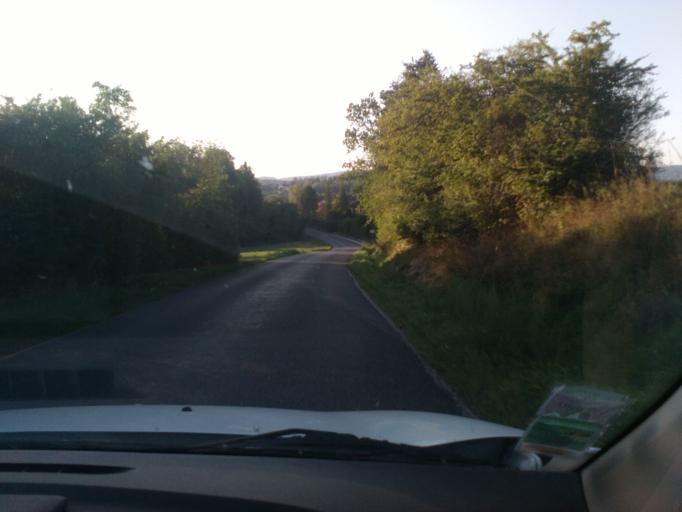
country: FR
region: Lorraine
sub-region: Departement des Vosges
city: Saint-Michel-sur-Meurthe
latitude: 48.3135
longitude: 6.8926
